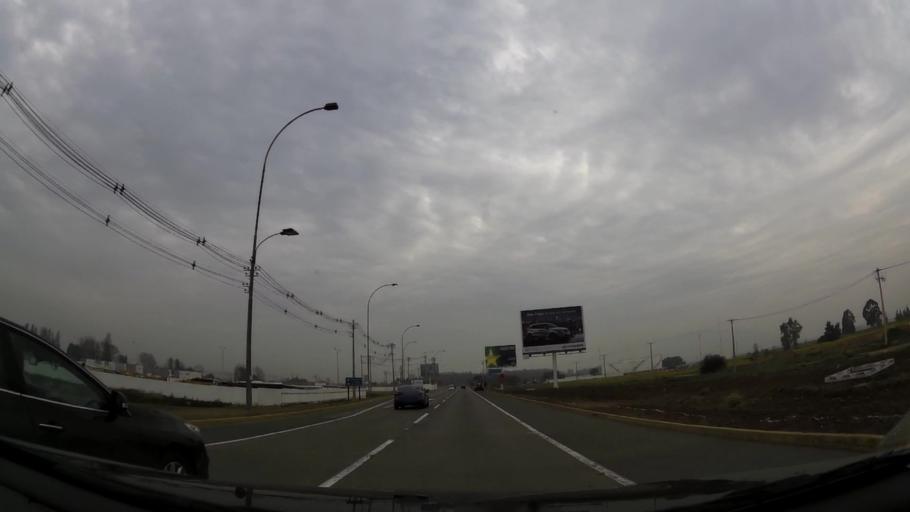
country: CL
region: Santiago Metropolitan
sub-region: Provincia de Santiago
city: Lo Prado
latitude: -33.4067
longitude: -70.7947
